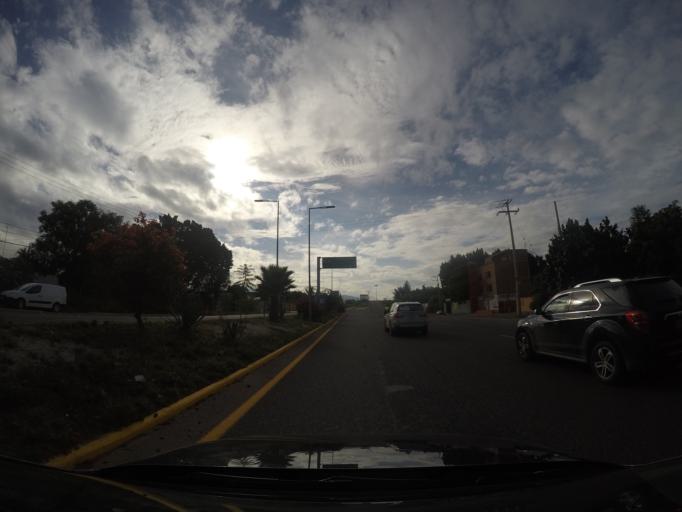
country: MX
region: Oaxaca
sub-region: Santa Cruz Amilpas
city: Santa Cruz Amilpas
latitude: 17.0612
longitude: -96.6657
